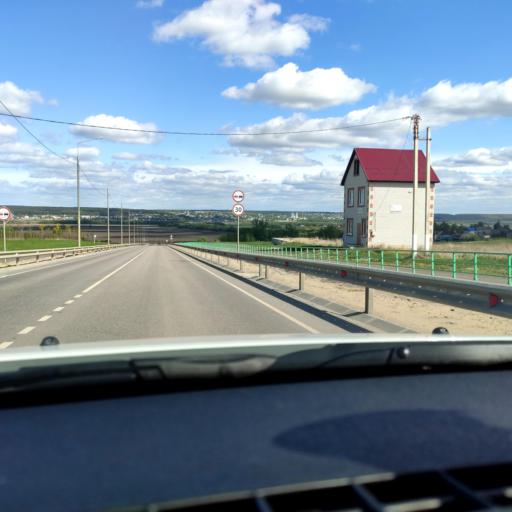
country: RU
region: Lipetsk
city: Zadonsk
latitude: 52.4135
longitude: 38.8700
